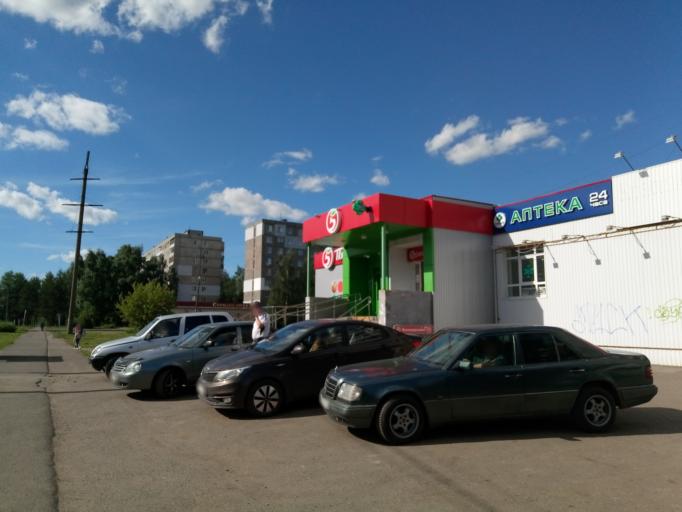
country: RU
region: Jaroslavl
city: Yaroslavl
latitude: 57.6424
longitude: 39.9446
